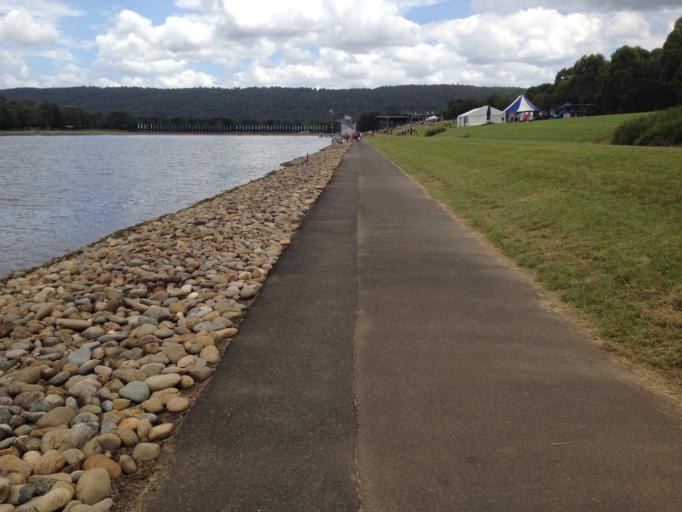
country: AU
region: New South Wales
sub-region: Penrith Municipality
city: Emu Heights
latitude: -33.7236
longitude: 150.6761
